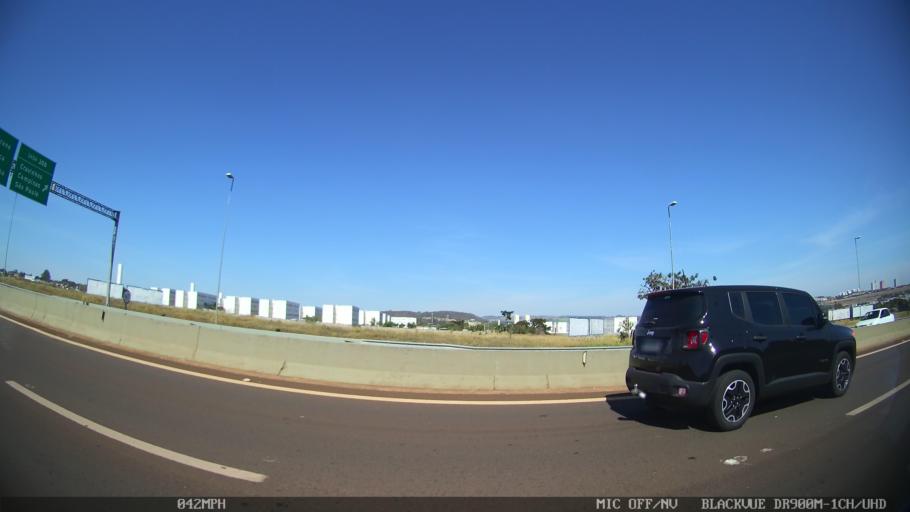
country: BR
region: Sao Paulo
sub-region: Ribeirao Preto
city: Ribeirao Preto
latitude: -21.2083
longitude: -47.7644
